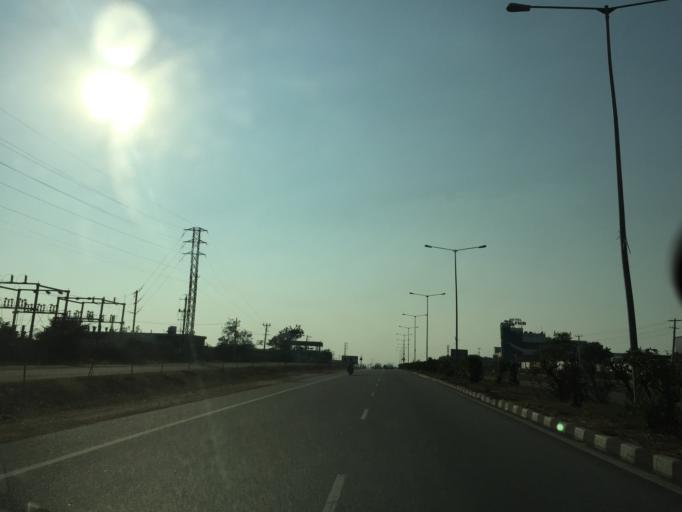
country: IN
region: Telangana
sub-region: Nalgonda
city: Bhongir
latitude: 17.5043
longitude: 78.8632
